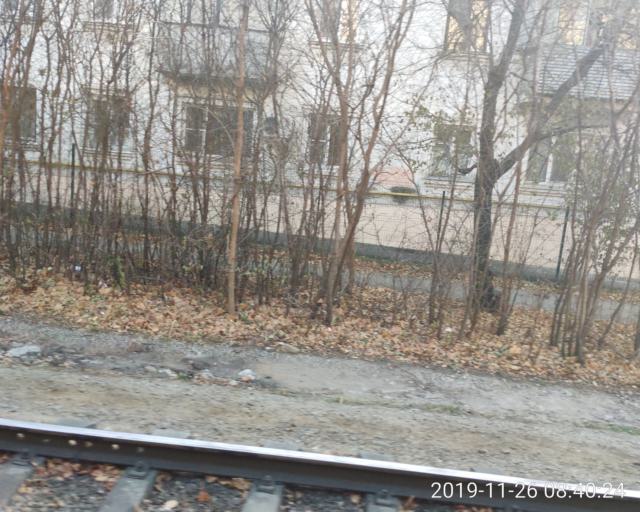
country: RU
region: Krasnodarskiy
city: Krasnodar
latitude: 45.0554
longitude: 38.9842
